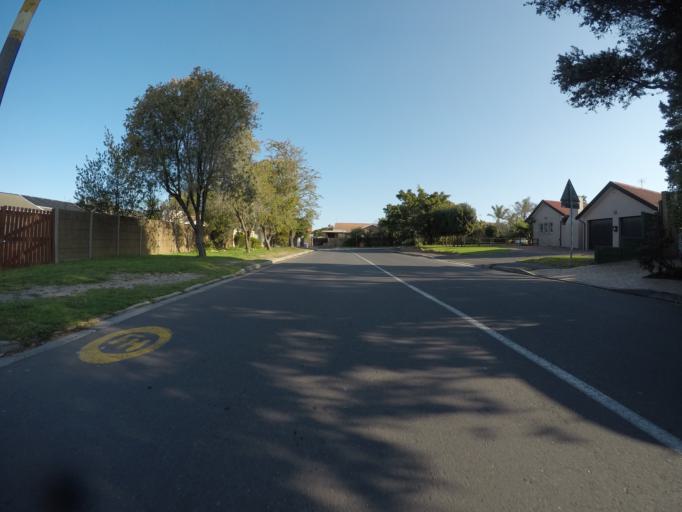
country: ZA
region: Western Cape
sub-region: City of Cape Town
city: Kraaifontein
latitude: -33.8548
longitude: 18.6573
